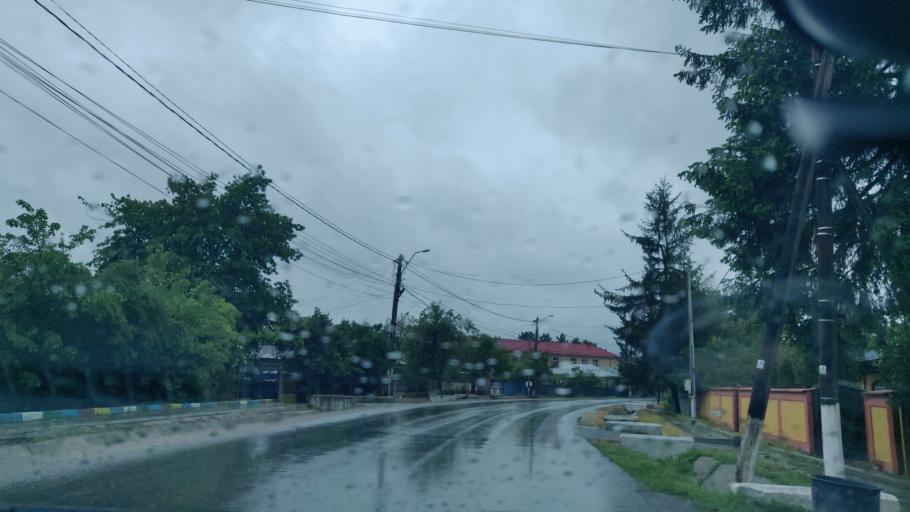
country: RO
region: Giurgiu
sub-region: Comuna Bulbucata
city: Bulbucata
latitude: 44.2831
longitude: 25.8082
